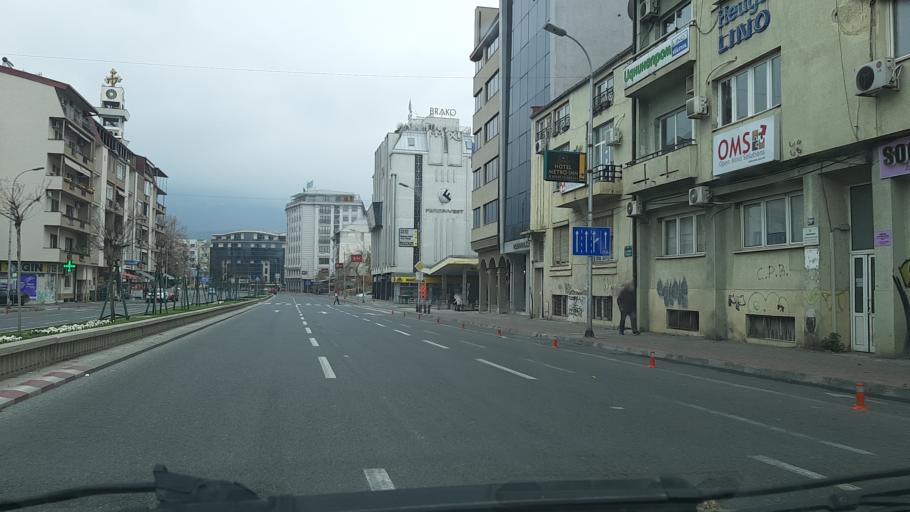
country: MK
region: Karpos
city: Skopje
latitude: 42.0003
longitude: 21.4270
